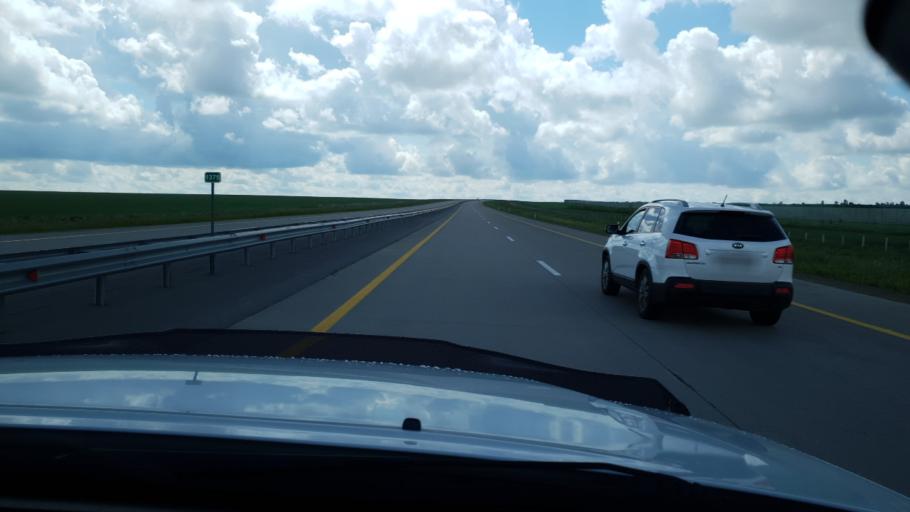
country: KZ
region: Qaraghandy
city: Osakarovka
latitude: 50.5424
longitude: 72.6422
